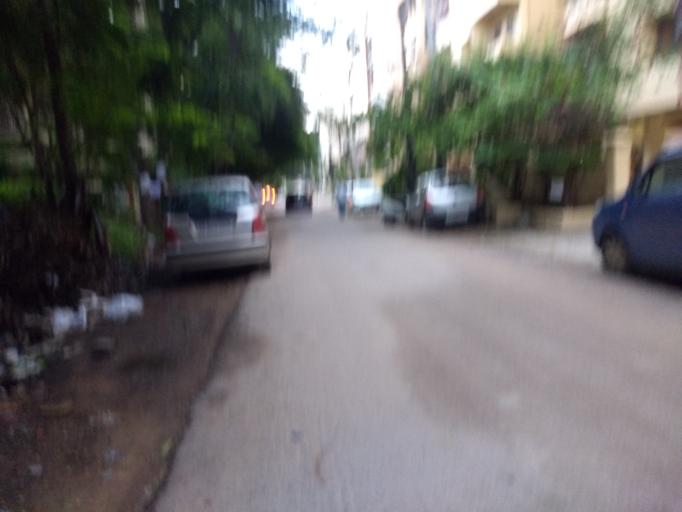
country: IN
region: Telangana
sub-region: Rangareddi
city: Kukatpalli
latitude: 17.4879
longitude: 78.3859
